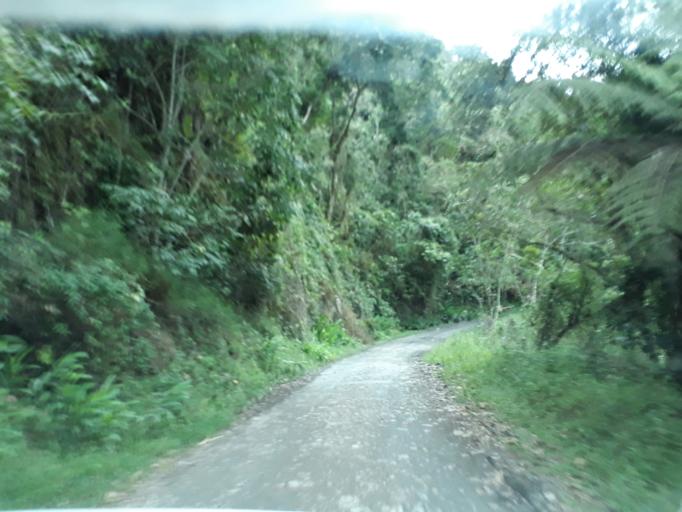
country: CO
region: Boyaca
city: Muzo
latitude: 5.3703
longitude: -74.0725
